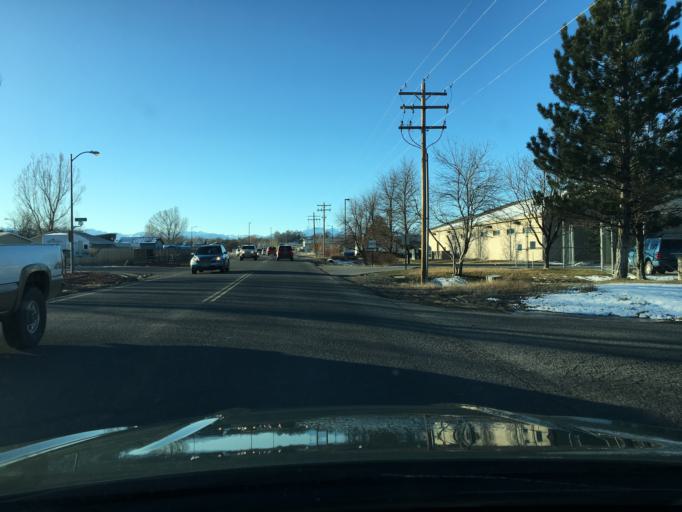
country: US
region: Colorado
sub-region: Montrose County
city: Montrose
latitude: 38.4527
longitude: -107.8637
